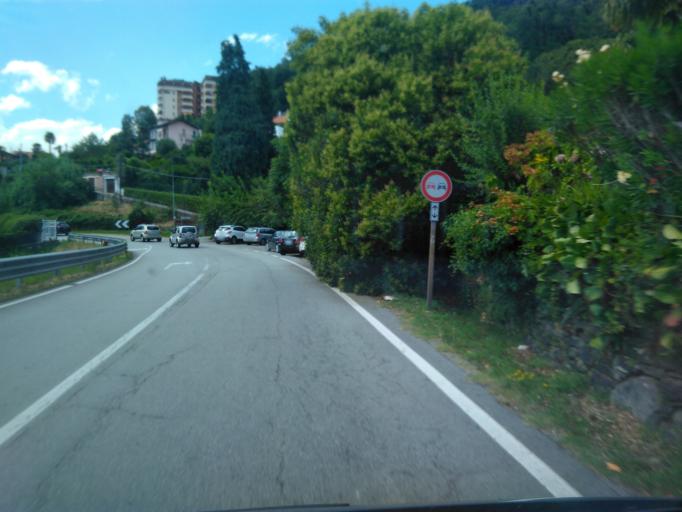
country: IT
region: Piedmont
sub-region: Provincia Verbano-Cusio-Ossola
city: Santino
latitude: 45.9364
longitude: 8.5235
